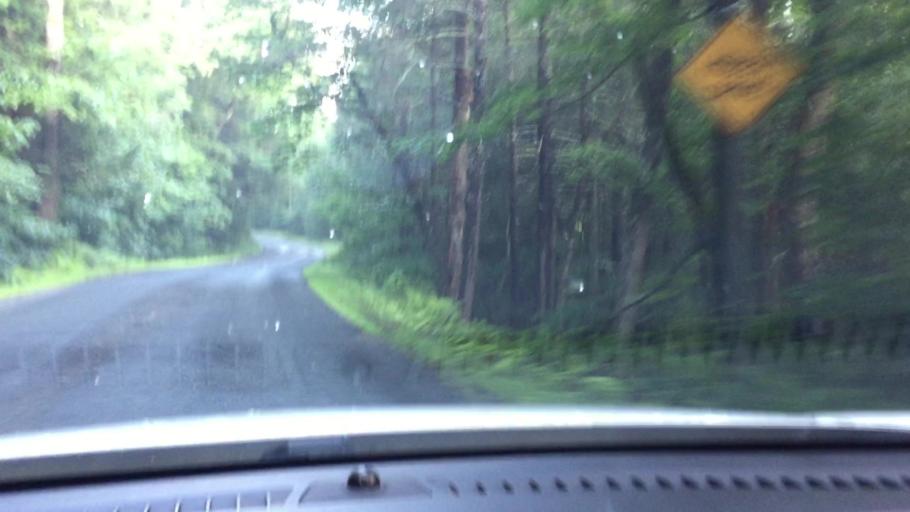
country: US
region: Massachusetts
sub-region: Berkshire County
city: Becket
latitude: 42.3746
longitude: -72.9712
